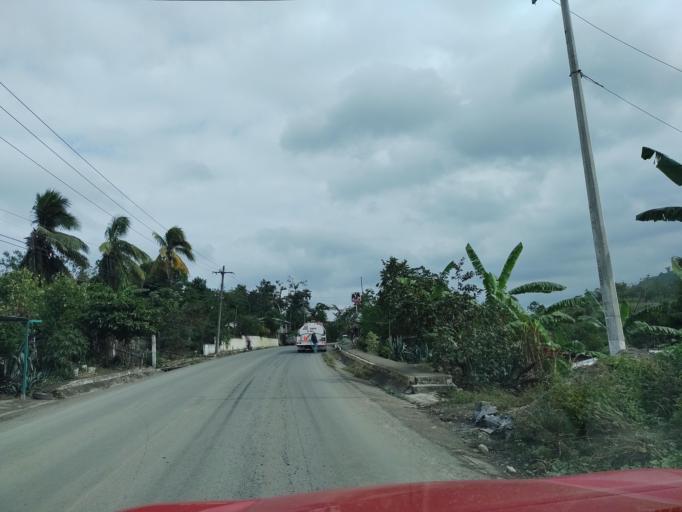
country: MX
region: Veracruz
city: Coatzintla
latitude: 20.4594
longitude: -97.4211
